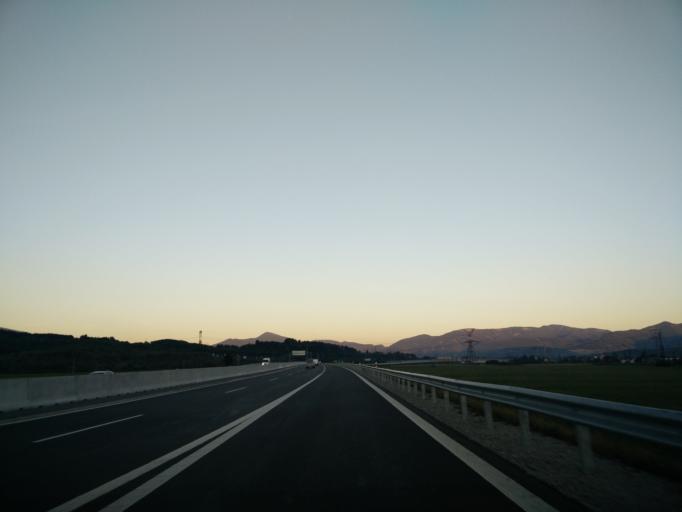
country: SK
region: Zilinsky
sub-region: Okres Zilina
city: Vrutky
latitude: 49.1085
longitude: 18.9607
